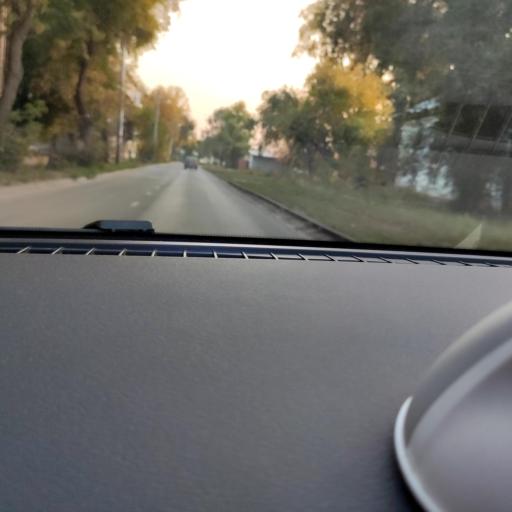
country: RU
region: Samara
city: Petra-Dubrava
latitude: 53.2306
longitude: 50.2848
